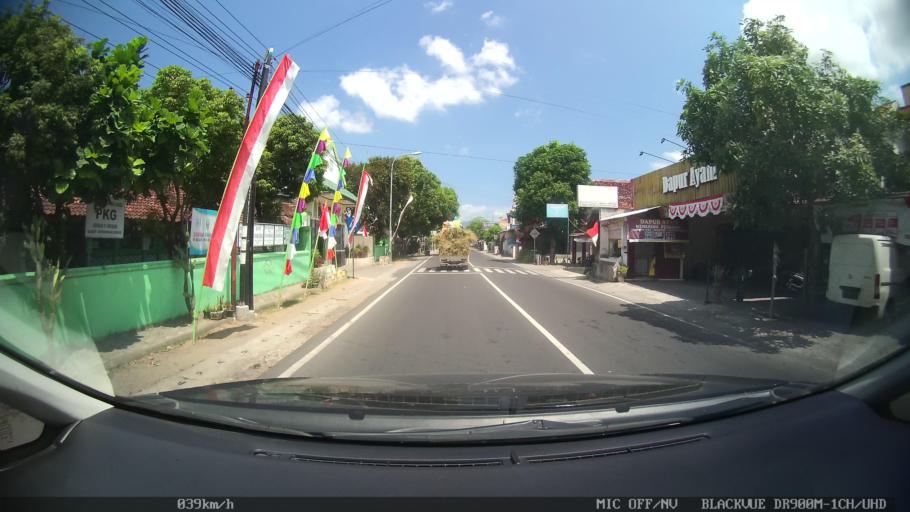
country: ID
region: Daerah Istimewa Yogyakarta
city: Sewon
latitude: -7.9081
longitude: 110.3832
